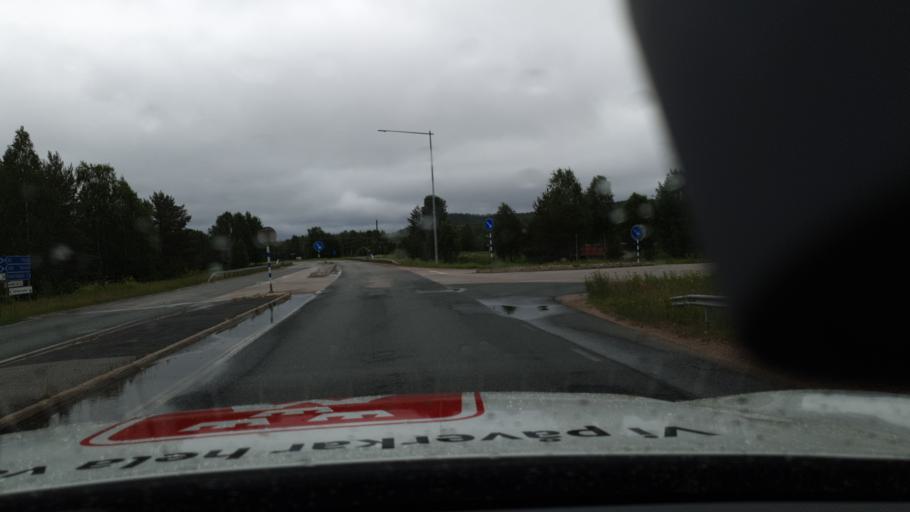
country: SE
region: Norrbotten
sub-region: Overtornea Kommun
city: OEvertornea
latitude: 66.3973
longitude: 23.6248
